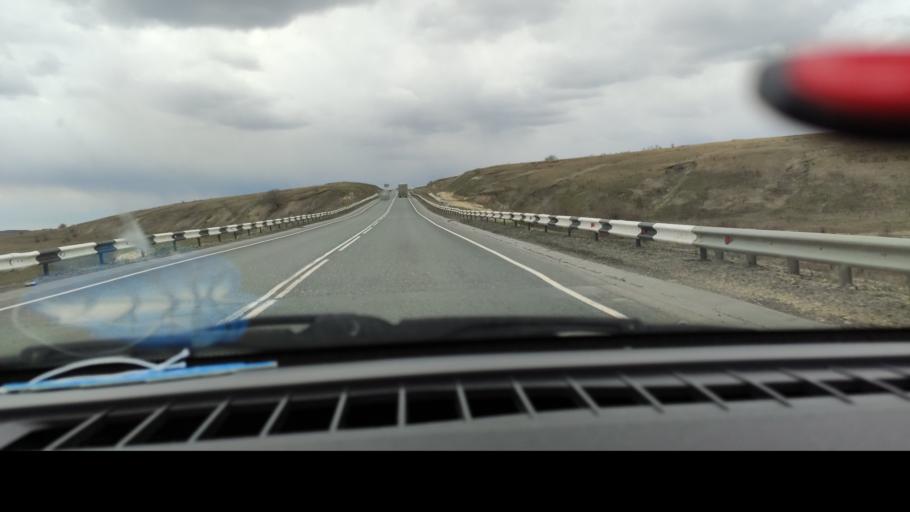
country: RU
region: Saratov
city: Sennoy
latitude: 52.1373
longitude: 46.8767
